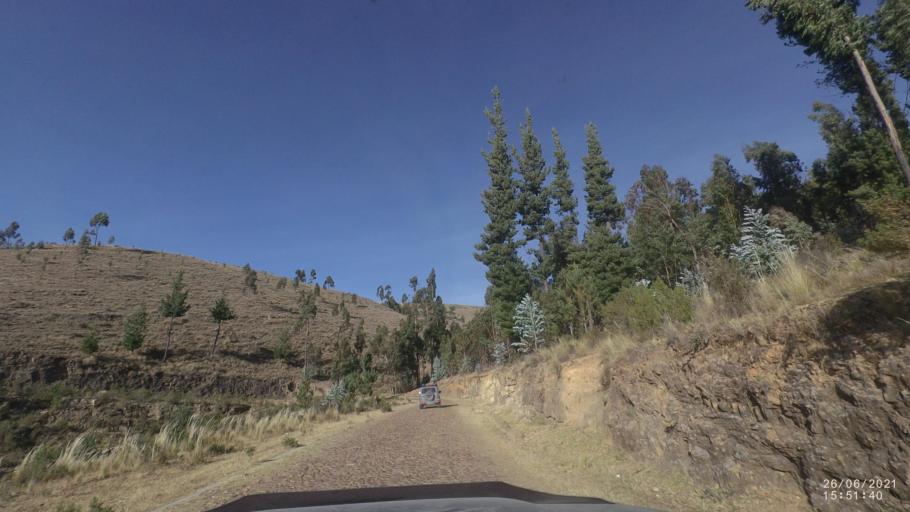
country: BO
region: Cochabamba
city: Arani
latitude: -17.8427
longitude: -65.7034
